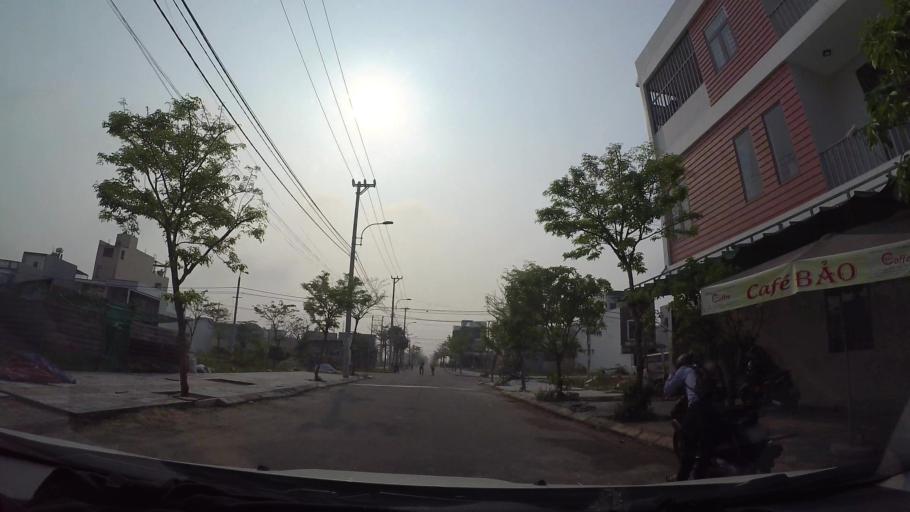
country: VN
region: Da Nang
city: Cam Le
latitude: 16.0079
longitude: 108.2278
